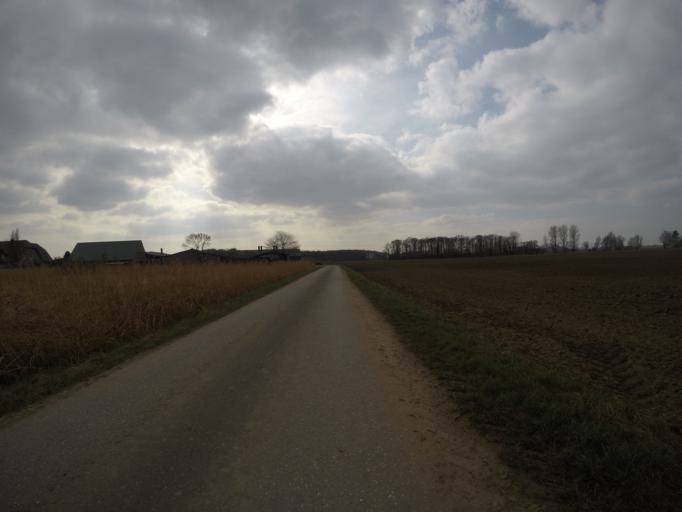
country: DE
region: North Rhine-Westphalia
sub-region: Regierungsbezirk Dusseldorf
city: Hamminkeln
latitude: 51.7898
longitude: 6.5687
